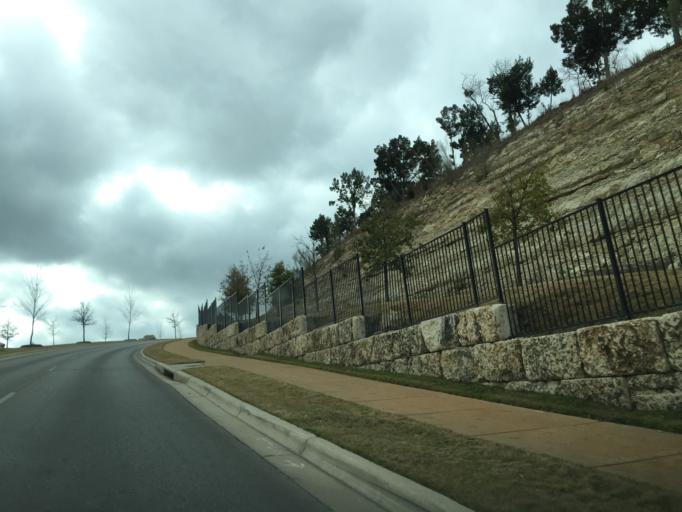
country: US
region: Texas
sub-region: Travis County
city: The Hills
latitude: 30.3523
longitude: -98.0061
